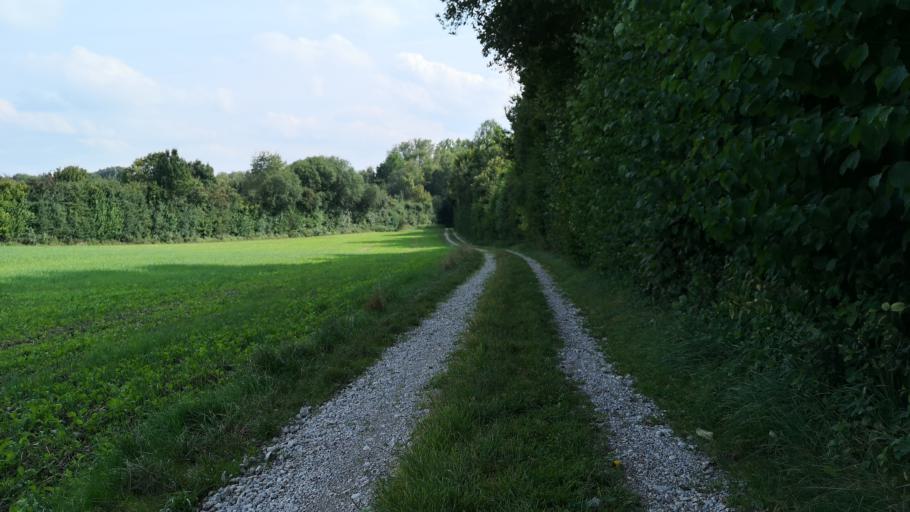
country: DE
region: Bavaria
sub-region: Upper Bavaria
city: Poing
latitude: 48.1770
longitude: 11.8180
